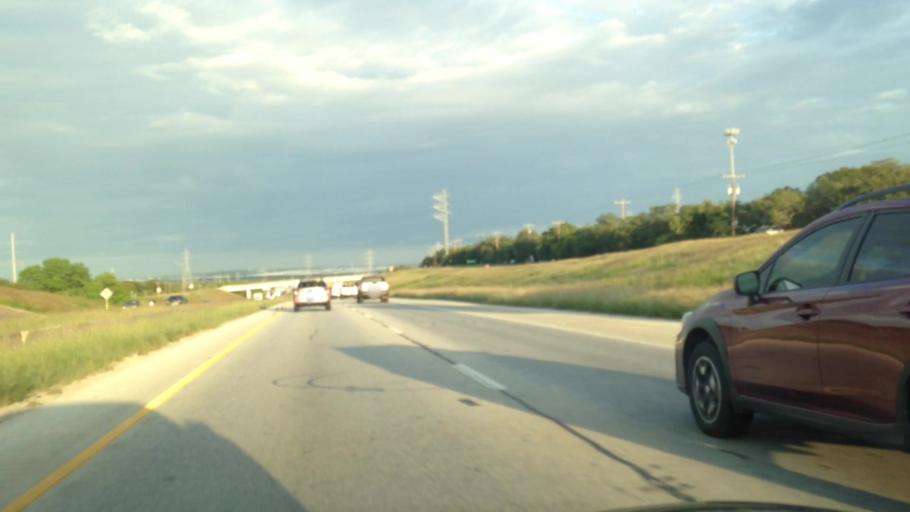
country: US
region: Texas
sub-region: Bexar County
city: Live Oak
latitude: 29.6026
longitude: -98.3713
